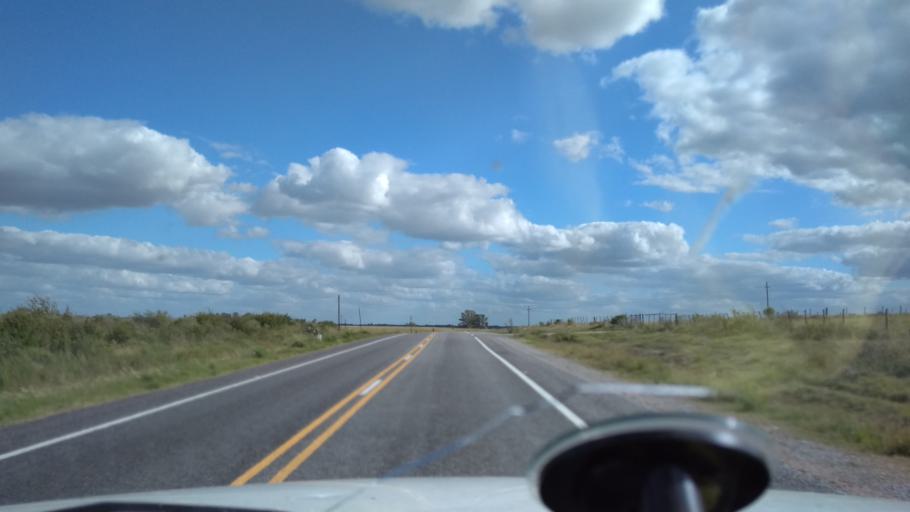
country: UY
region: Florida
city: Casupa
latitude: -34.0560
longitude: -55.6597
